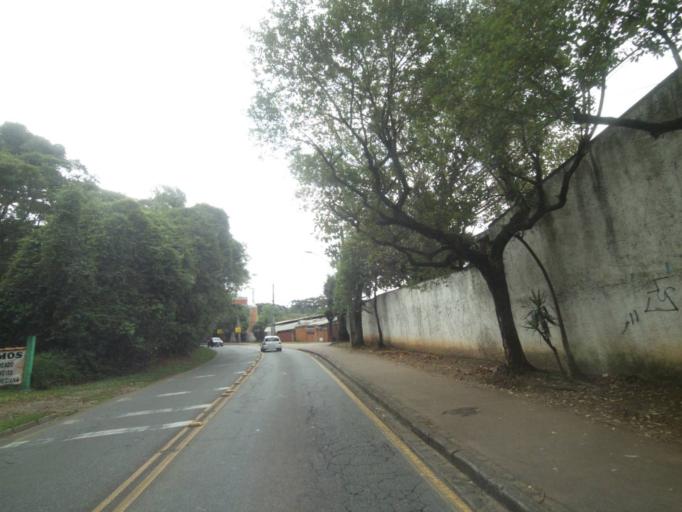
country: BR
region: Parana
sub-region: Curitiba
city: Curitiba
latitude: -25.3865
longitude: -49.2722
